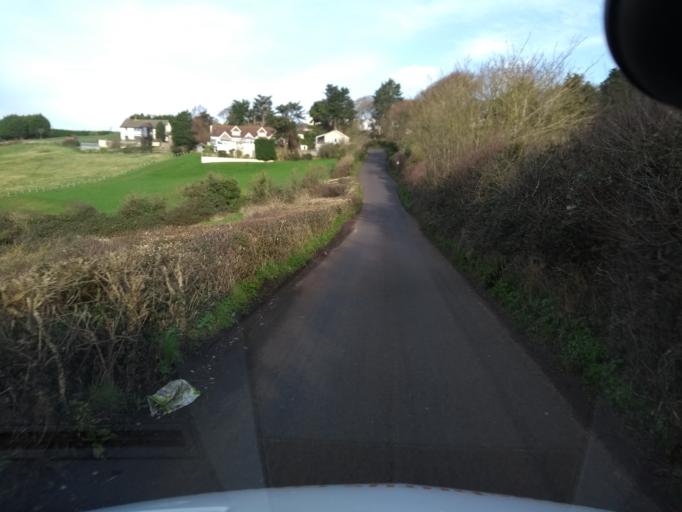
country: GB
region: England
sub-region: North Somerset
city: Bleadon
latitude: 51.3119
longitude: -2.9489
